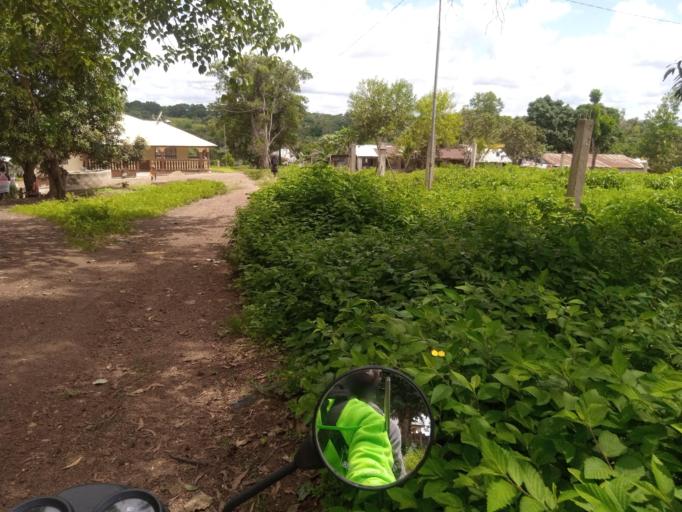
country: SL
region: Northern Province
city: Port Loko
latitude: 8.7588
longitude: -12.7792
